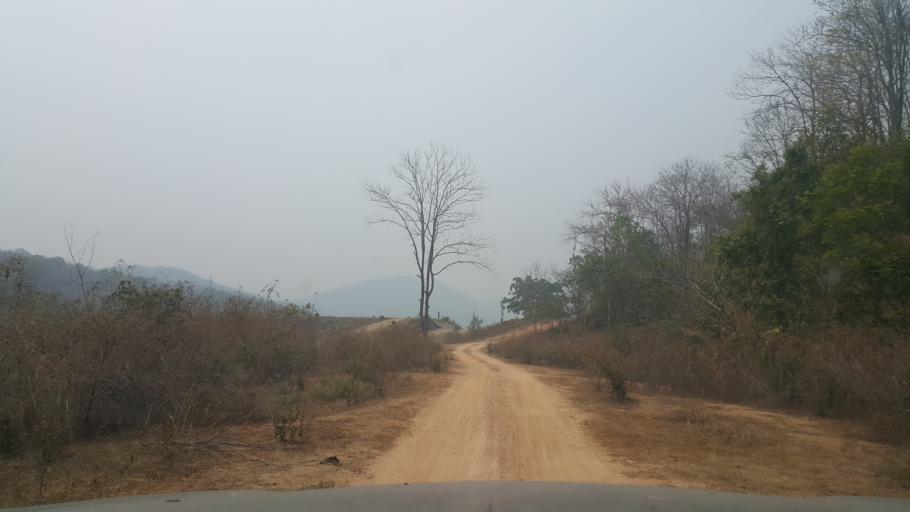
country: TH
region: Lampang
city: Hang Chat
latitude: 18.3214
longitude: 99.2452
